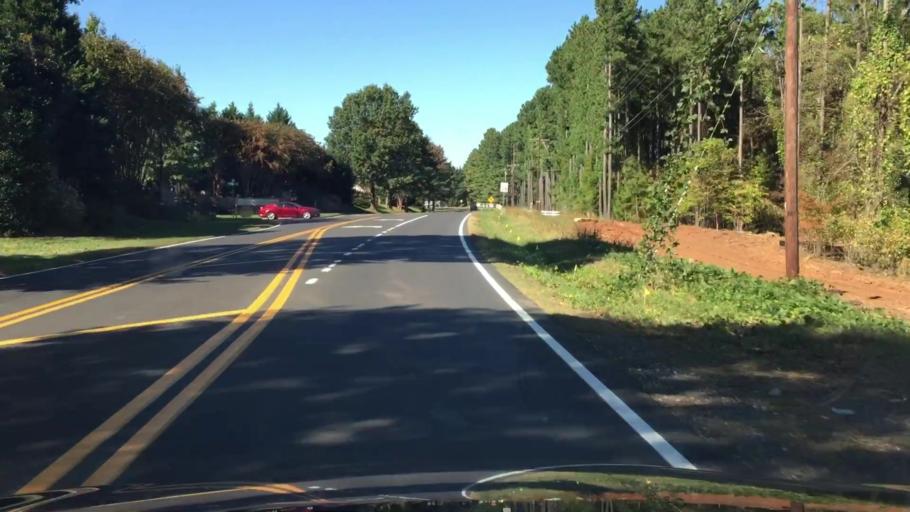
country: US
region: North Carolina
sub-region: Iredell County
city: Mooresville
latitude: 35.5827
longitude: -80.7835
